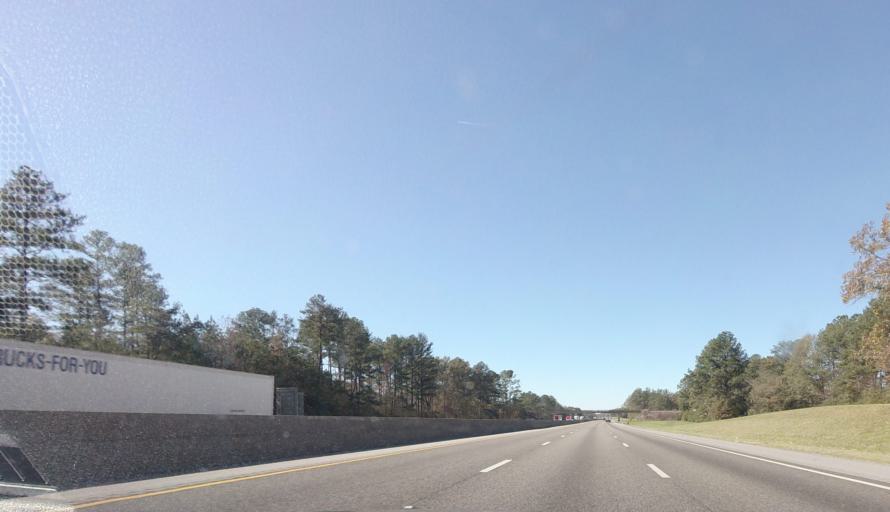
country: US
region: Alabama
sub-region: Calhoun County
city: Bynum
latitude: 33.5817
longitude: -85.9448
